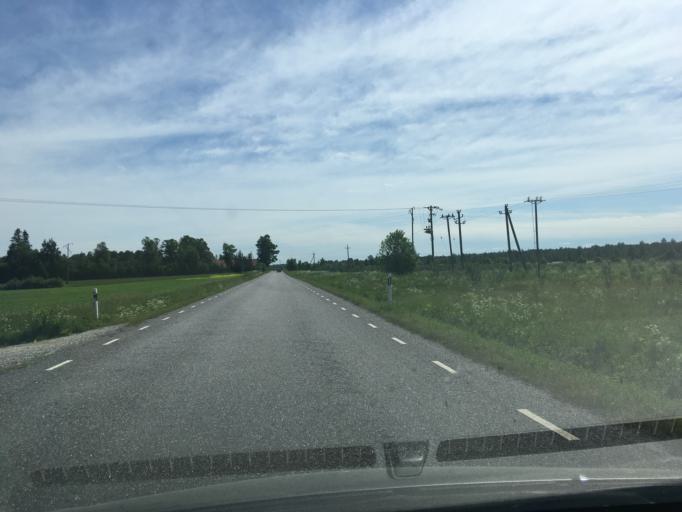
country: EE
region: Paernumaa
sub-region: Audru vald
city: Audru
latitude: 58.4302
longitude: 24.4030
